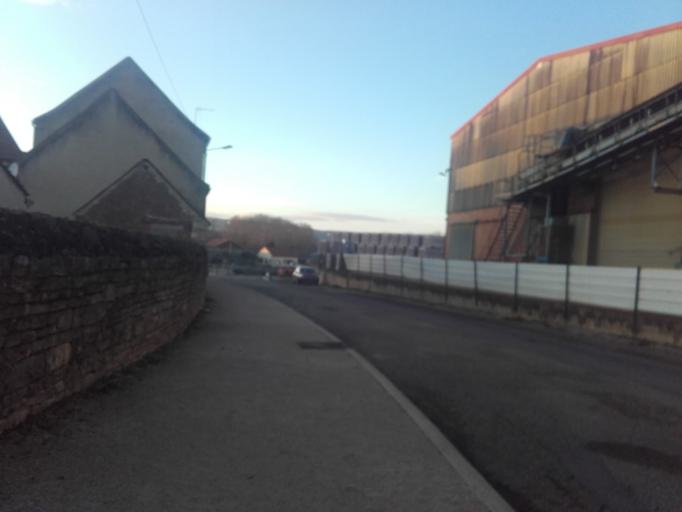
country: FR
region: Bourgogne
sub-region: Departement de Saone-et-Loire
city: Chagny
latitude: 46.9027
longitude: 4.7542
